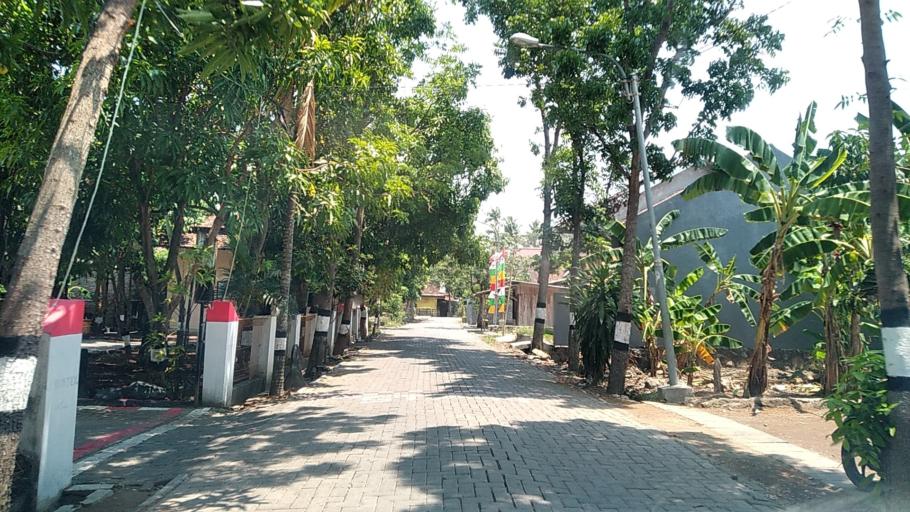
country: ID
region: Central Java
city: Mranggen
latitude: -7.0076
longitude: 110.4873
